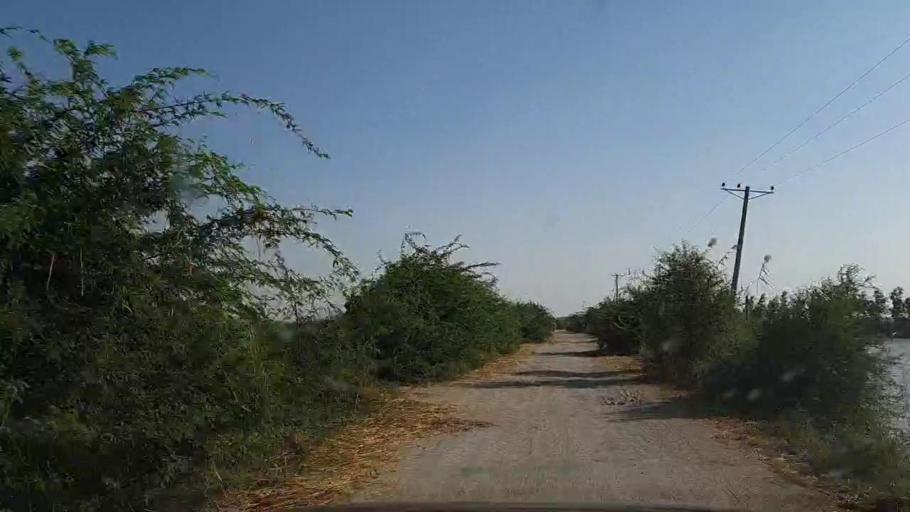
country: PK
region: Sindh
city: Thatta
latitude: 24.6395
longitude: 68.0759
